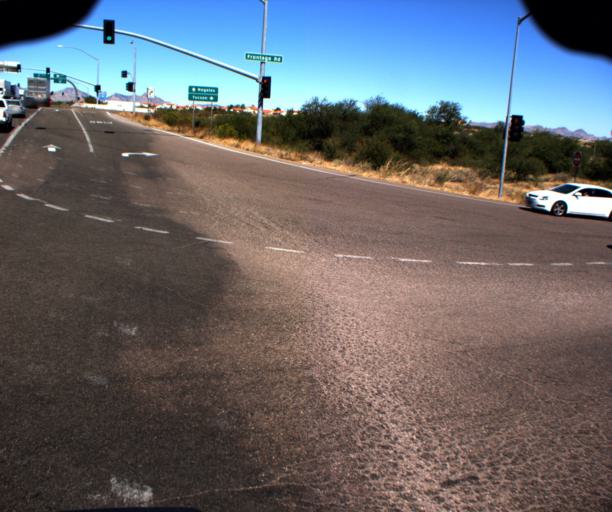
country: US
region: Arizona
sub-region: Santa Cruz County
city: Rio Rico
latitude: 31.4303
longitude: -110.9631
